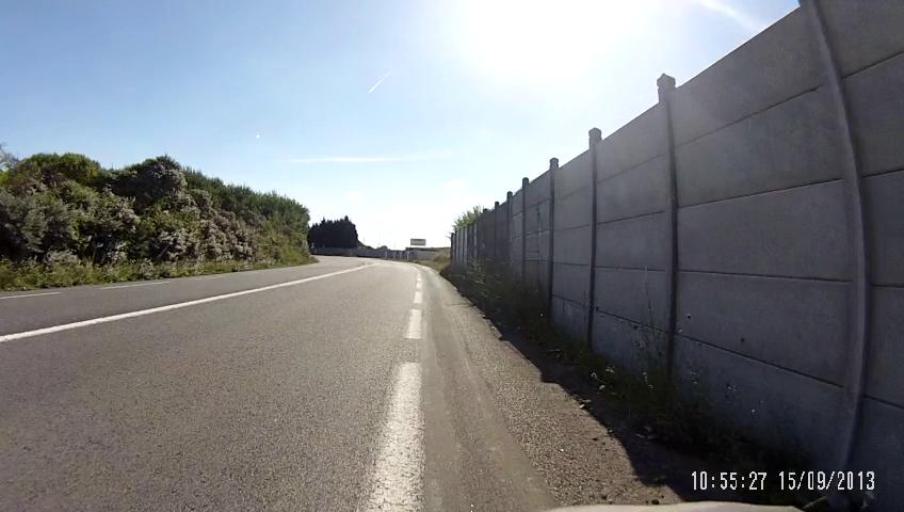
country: FR
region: Nord-Pas-de-Calais
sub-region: Departement du Nord
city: Zuydcoote
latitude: 51.0579
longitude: 2.4709
